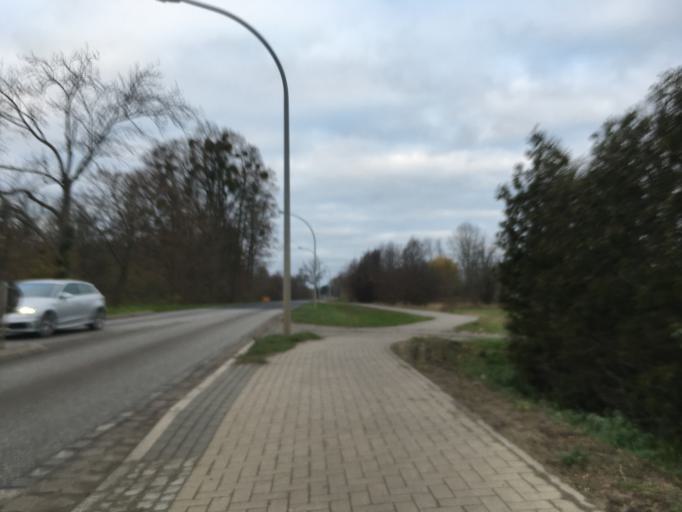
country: DE
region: Brandenburg
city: Seelow
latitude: 52.5751
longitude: 14.3486
